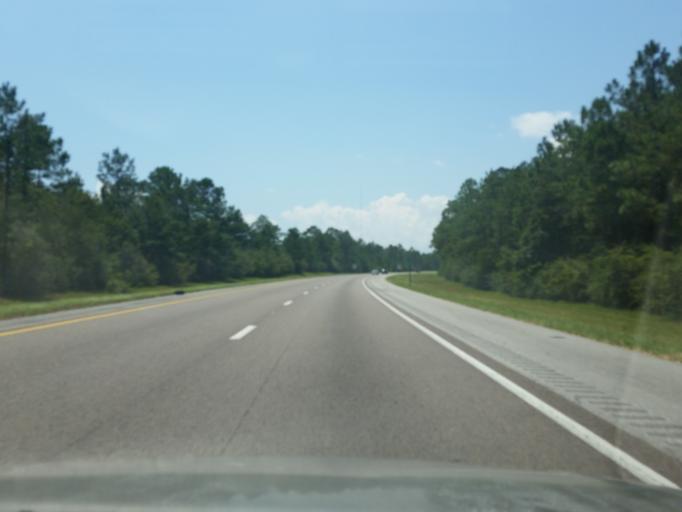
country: US
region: Florida
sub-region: Escambia County
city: Cantonment
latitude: 30.5814
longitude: -87.5150
